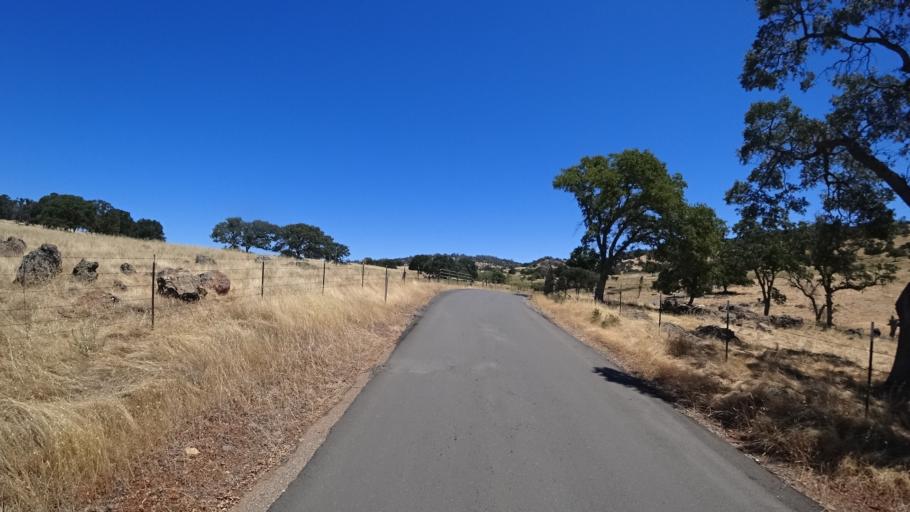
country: US
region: California
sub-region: Calaveras County
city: Rancho Calaveras
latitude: 38.0497
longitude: -120.8176
